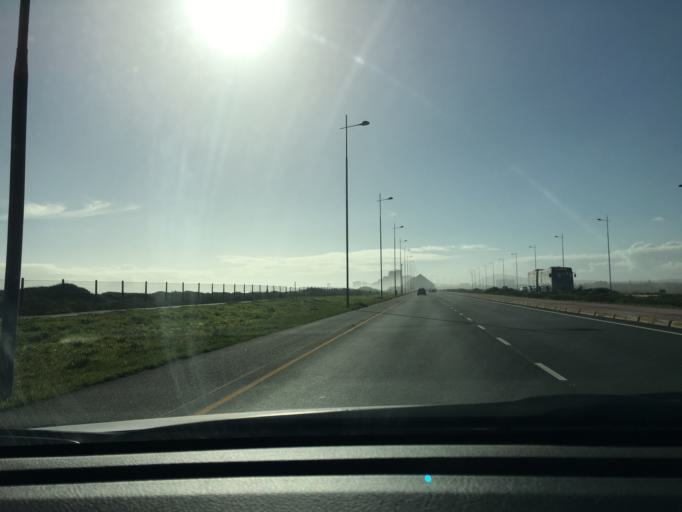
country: ZA
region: Western Cape
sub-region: City of Cape Town
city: Sunset Beach
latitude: -33.8392
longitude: 18.4858
